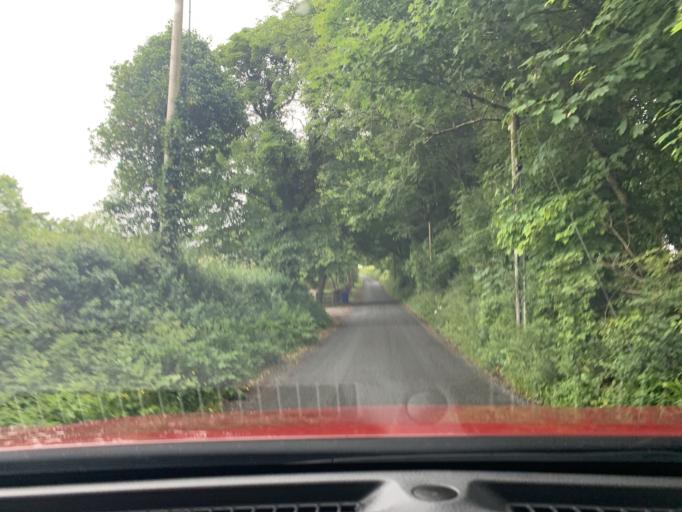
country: IE
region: Connaught
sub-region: Sligo
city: Sligo
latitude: 54.3034
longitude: -8.4568
